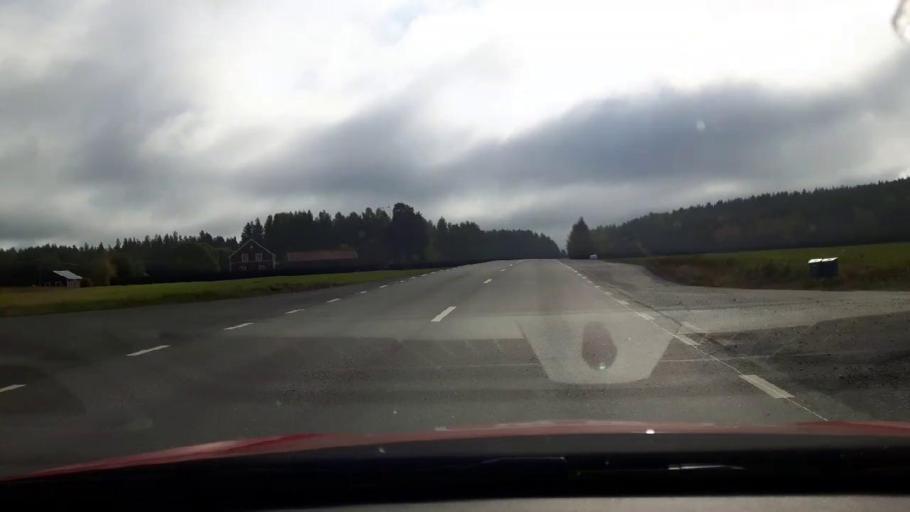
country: SE
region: Gaevleborg
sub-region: Ljusdals Kommun
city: Farila
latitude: 61.8768
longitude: 15.7184
